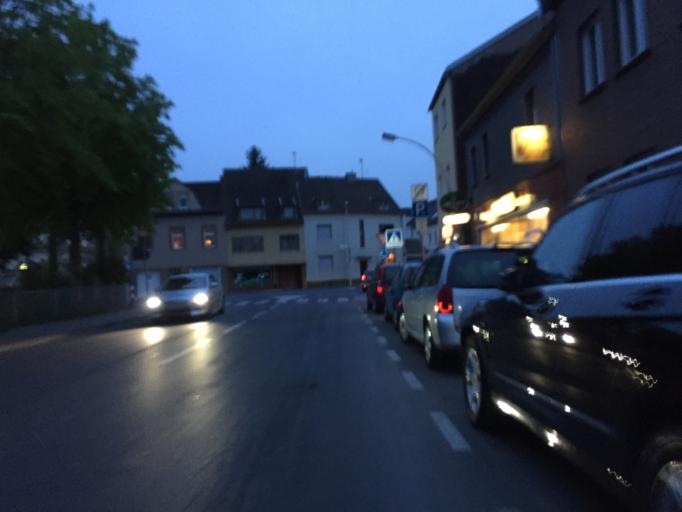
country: DE
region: North Rhine-Westphalia
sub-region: Regierungsbezirk Koln
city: Alfter
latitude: 50.7367
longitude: 7.0479
